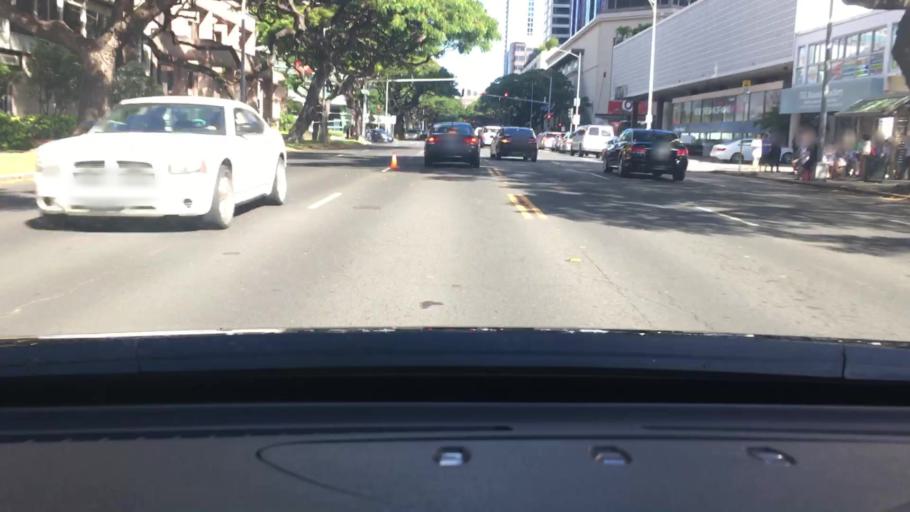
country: US
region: Hawaii
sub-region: Honolulu County
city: Honolulu
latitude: 21.2936
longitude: -157.8435
